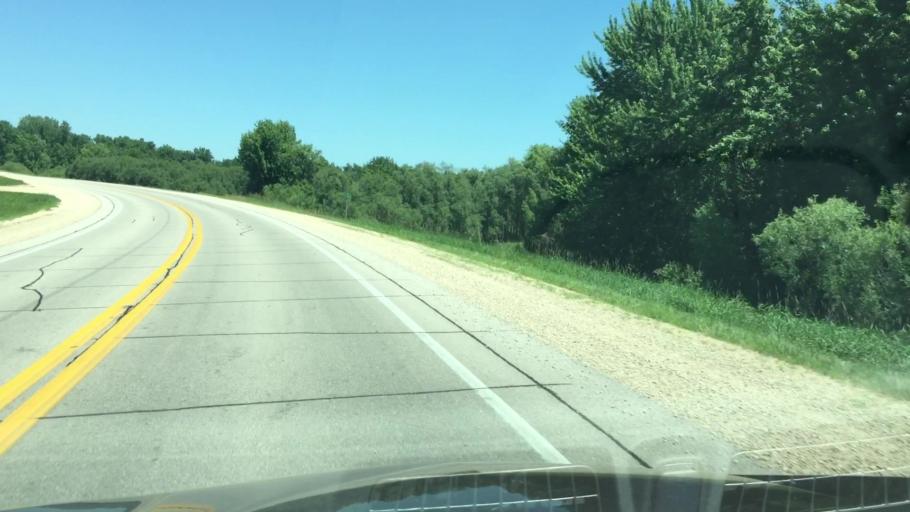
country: US
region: Iowa
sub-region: Cedar County
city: Mechanicsville
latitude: 42.0112
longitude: -91.1370
